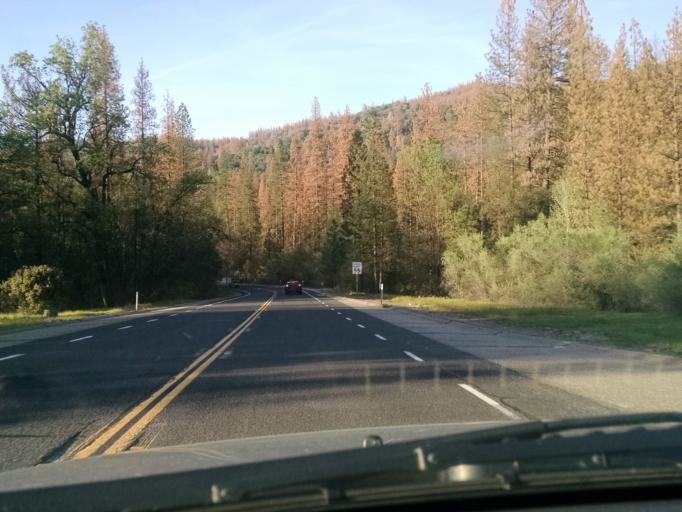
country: US
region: California
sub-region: Madera County
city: Ahwahnee
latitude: 37.4225
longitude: -119.7250
